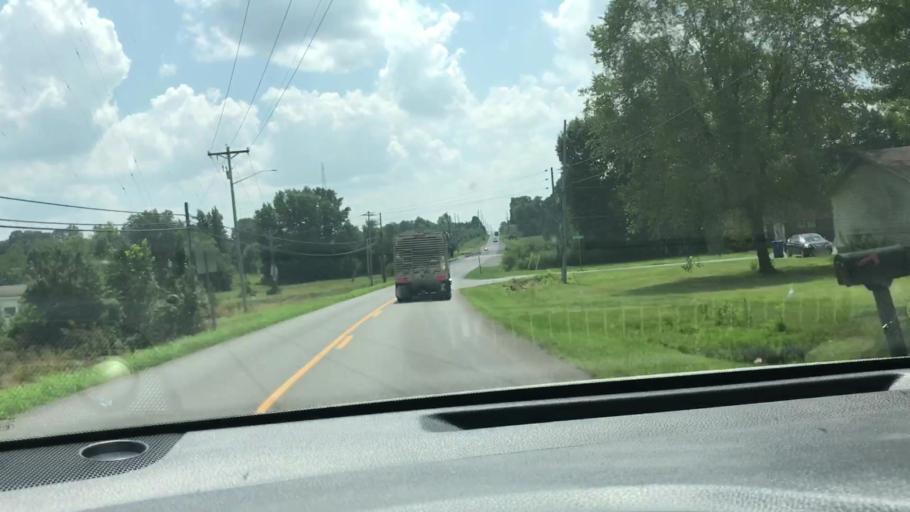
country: US
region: Kentucky
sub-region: Calloway County
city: Murray
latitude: 36.6292
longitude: -88.3019
